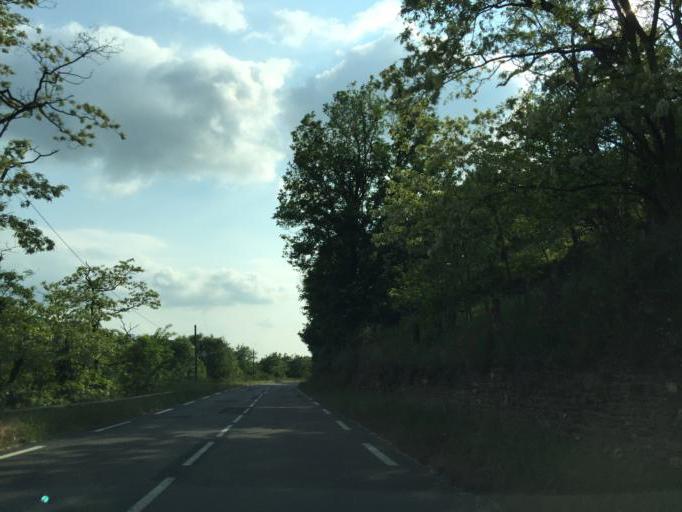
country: FR
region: Rhone-Alpes
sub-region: Departement du Rhone
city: Echalas
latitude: 45.5602
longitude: 4.6925
